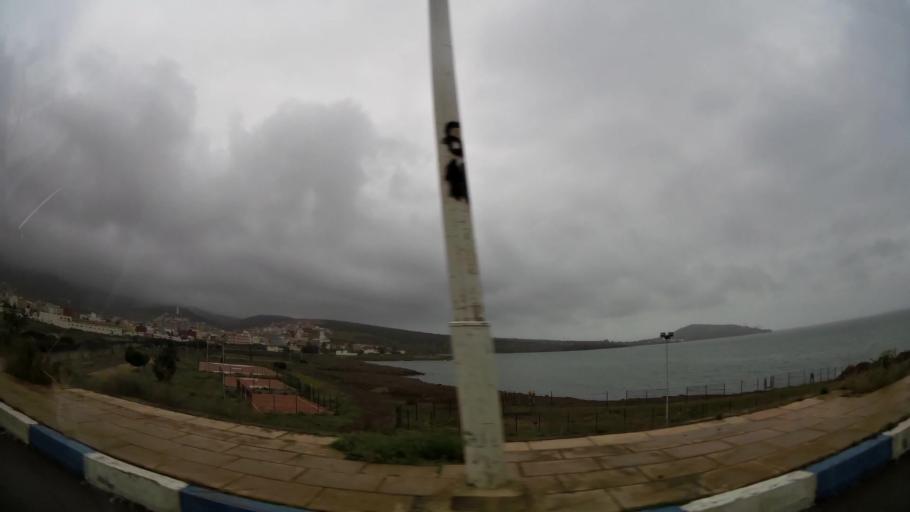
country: MA
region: Oriental
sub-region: Nador
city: Nador
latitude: 35.1901
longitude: -2.9264
